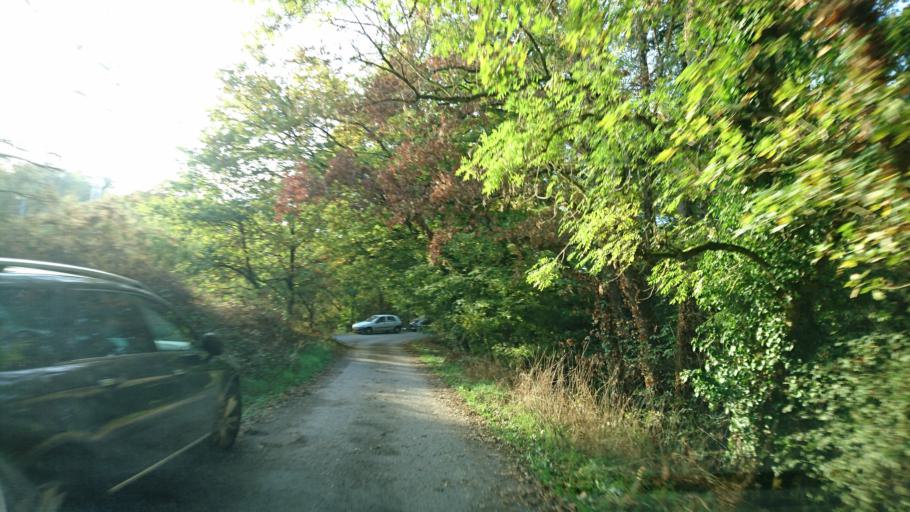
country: FR
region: Brittany
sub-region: Departement d'Ille-et-Vilaine
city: Bruz
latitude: 47.9966
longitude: -1.7509
